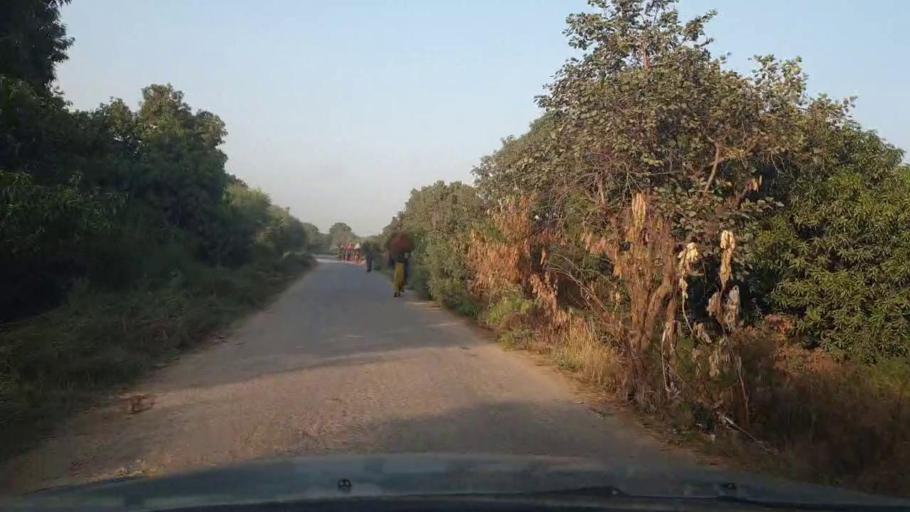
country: PK
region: Sindh
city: Tando Jam
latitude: 25.4165
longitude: 68.4889
